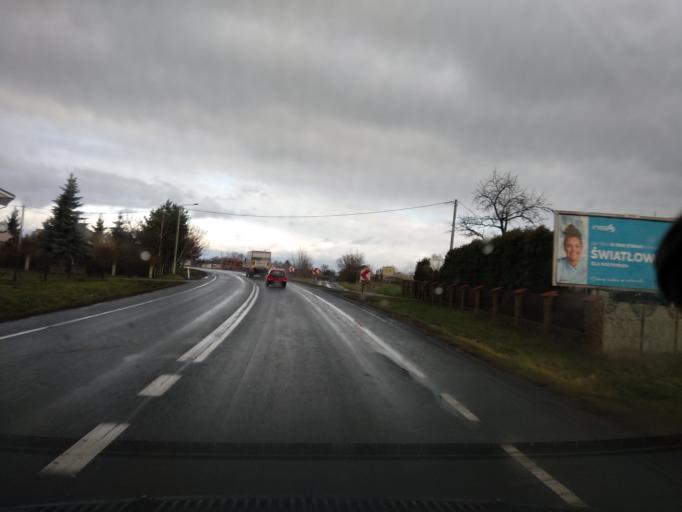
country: PL
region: Greater Poland Voivodeship
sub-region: Powiat koninski
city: Stare Miasto
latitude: 52.1522
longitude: 18.2043
